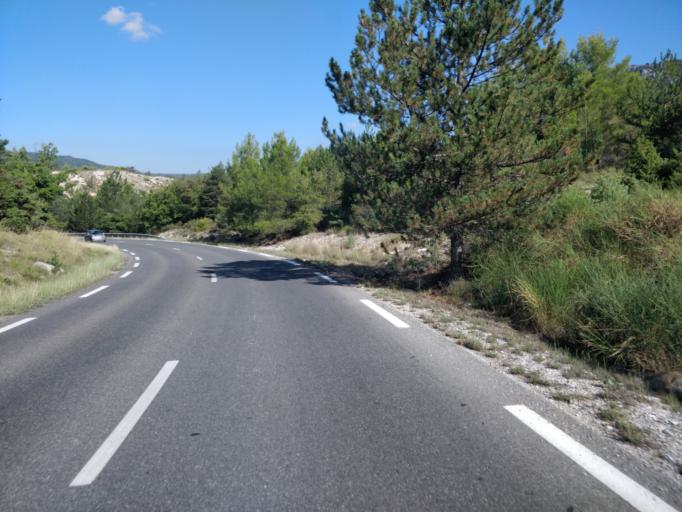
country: FR
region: Provence-Alpes-Cote d'Azur
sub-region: Departement des Alpes-de-Haute-Provence
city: Riez
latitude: 43.8078
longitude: 6.2347
